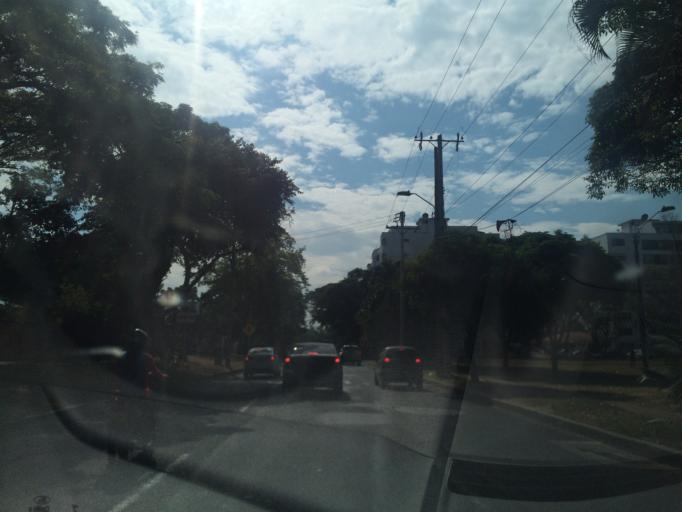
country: CO
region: Valle del Cauca
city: Cali
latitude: 3.3936
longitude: -76.5408
